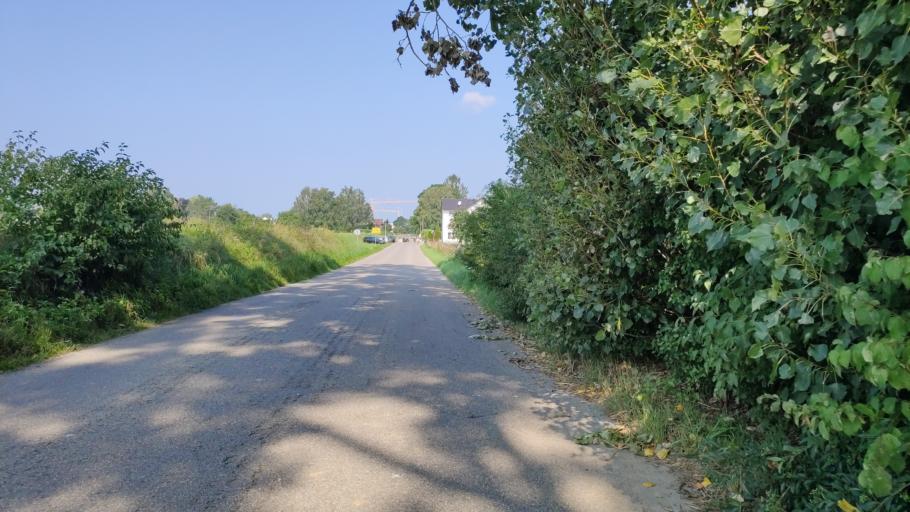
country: DE
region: Bavaria
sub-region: Swabia
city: Bobingen
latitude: 48.2596
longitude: 10.8372
